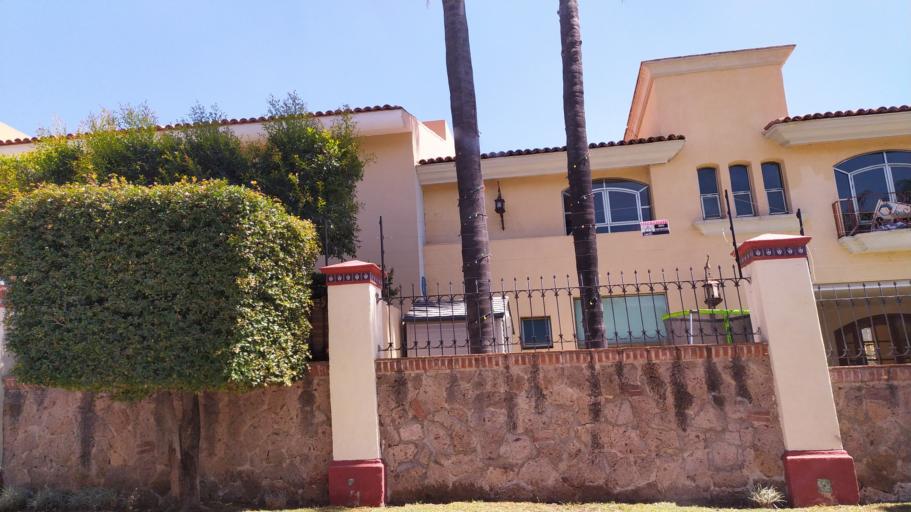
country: MX
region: Jalisco
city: Zapopan2
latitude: 20.6957
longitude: -103.4379
